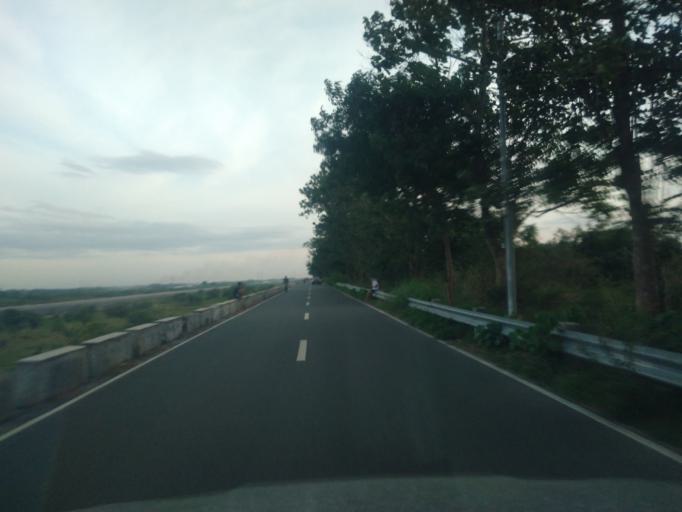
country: PH
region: Central Luzon
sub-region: Province of Pampanga
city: Santa Rita
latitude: 15.0144
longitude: 120.6243
